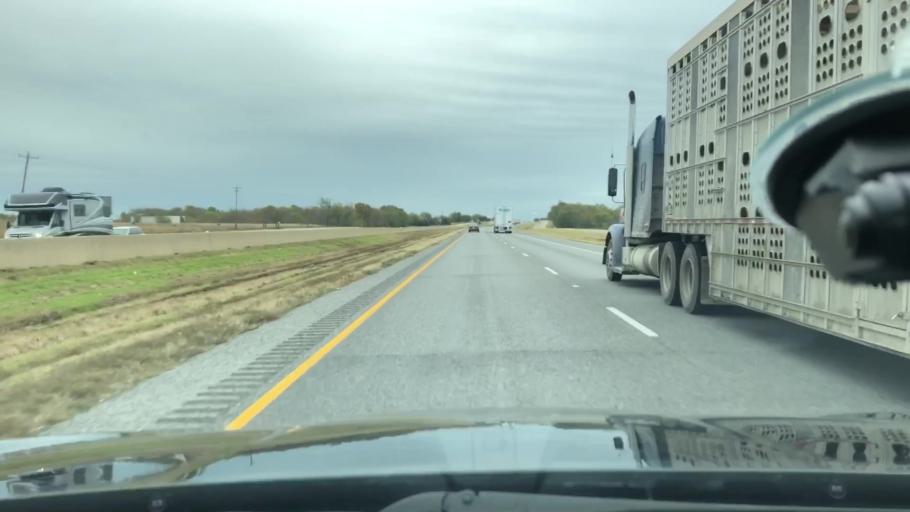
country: US
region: Texas
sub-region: Hunt County
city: Commerce
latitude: 33.1313
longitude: -95.9115
